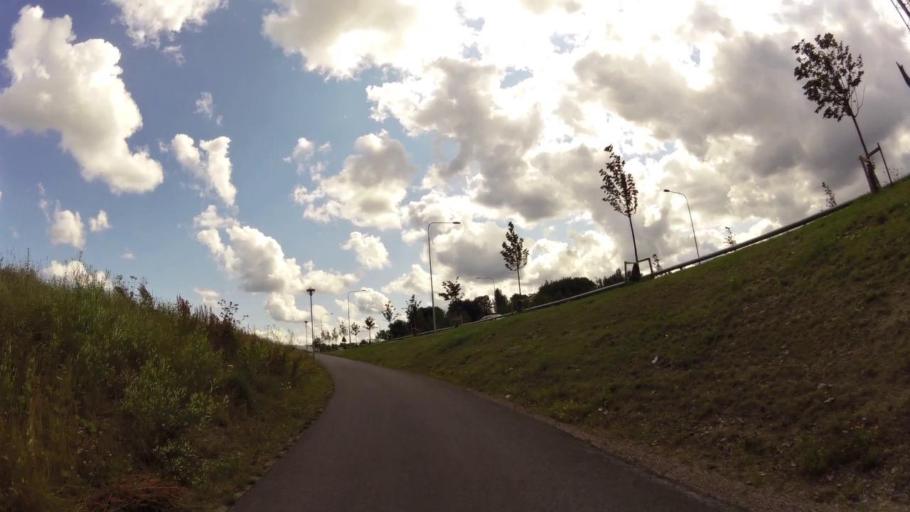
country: SE
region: OEstergoetland
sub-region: Linkopings Kommun
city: Linkoping
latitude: 58.4119
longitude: 15.6537
